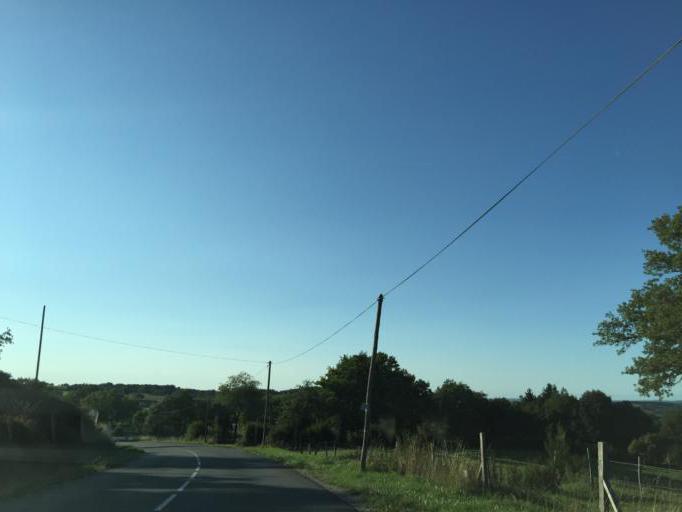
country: FR
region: Midi-Pyrenees
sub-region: Departement de l'Aveyron
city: Salles-Curan
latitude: 44.1706
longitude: 2.7921
